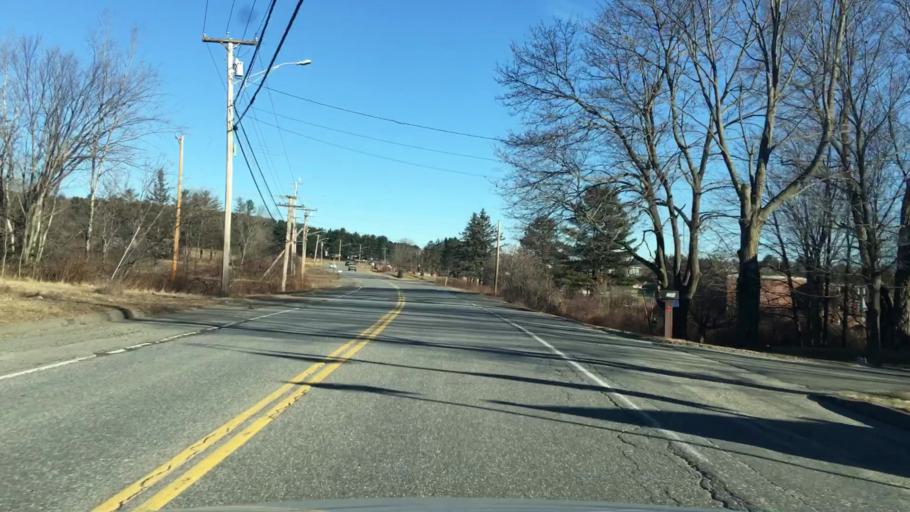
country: US
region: Maine
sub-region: Kennebec County
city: Waterville
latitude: 44.5228
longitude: -69.6670
